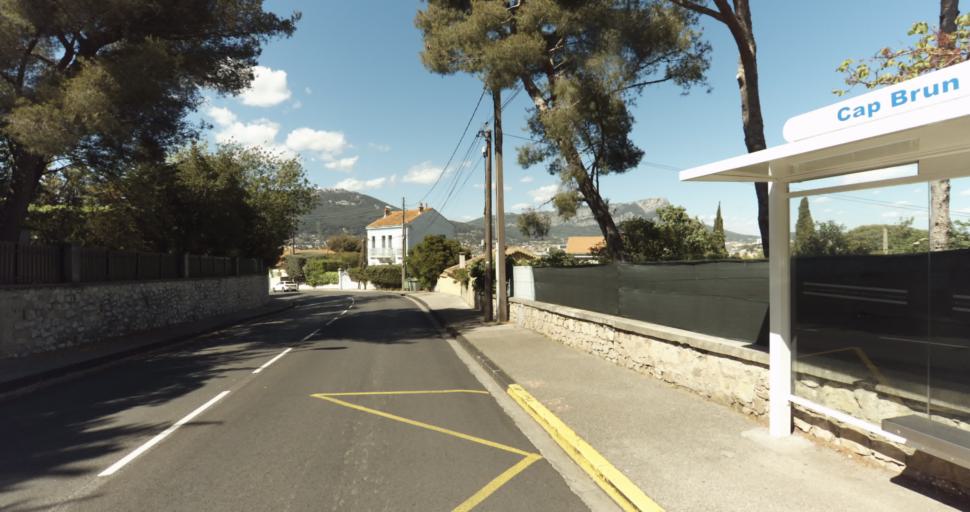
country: FR
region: Provence-Alpes-Cote d'Azur
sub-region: Departement du Var
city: La Valette-du-Var
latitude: 43.1110
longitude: 5.9691
